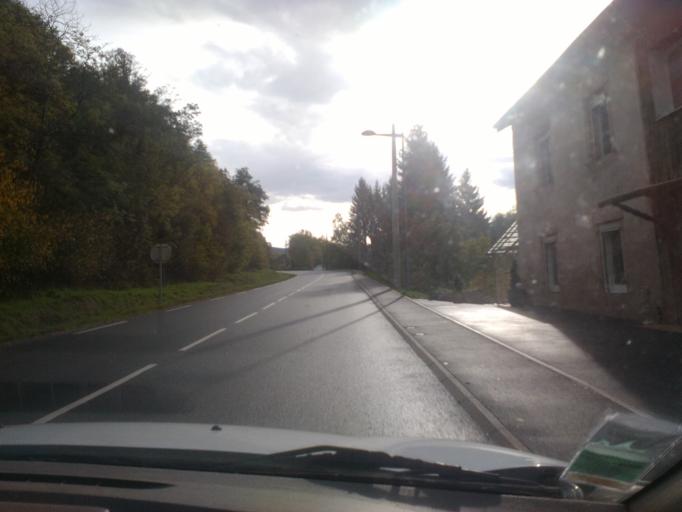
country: FR
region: Lorraine
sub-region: Departement des Vosges
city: Corcieux
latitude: 48.1674
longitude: 6.8919
